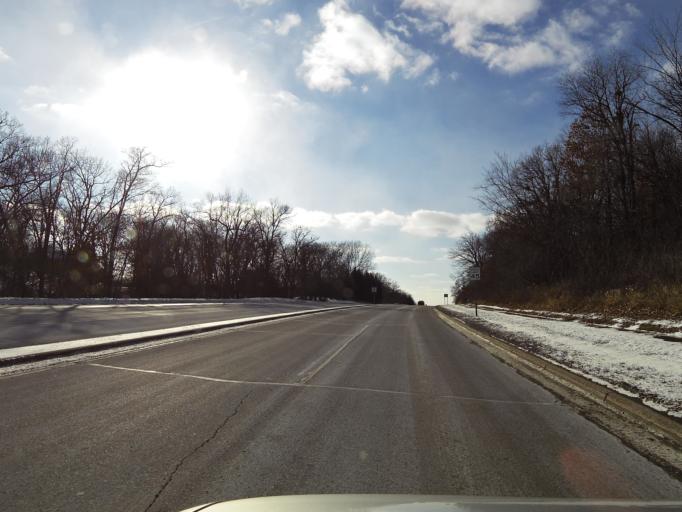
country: US
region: Minnesota
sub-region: Dakota County
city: Apple Valley
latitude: 44.7559
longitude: -93.2322
